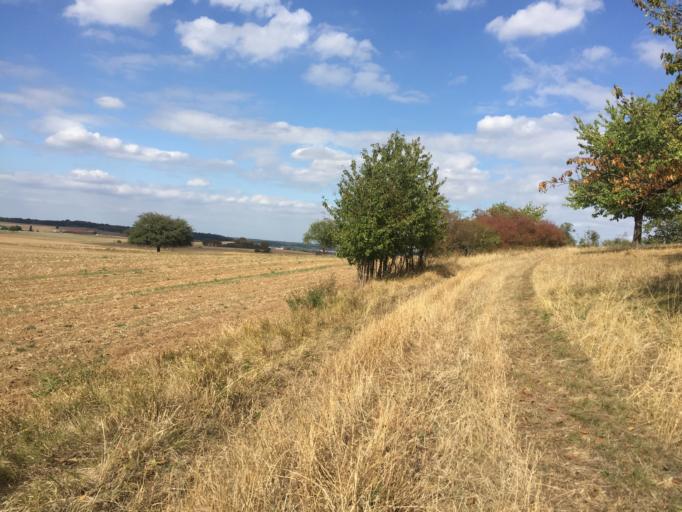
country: DE
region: Hesse
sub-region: Regierungsbezirk Giessen
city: Lich
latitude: 50.4849
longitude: 8.8291
